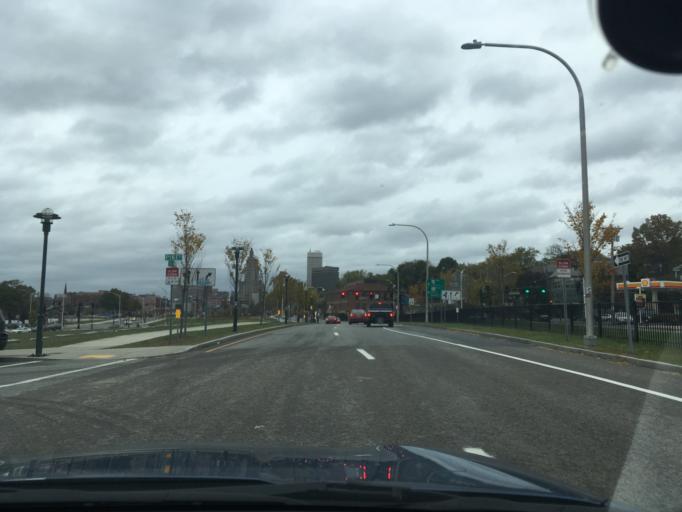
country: US
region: Rhode Island
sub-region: Providence County
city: Providence
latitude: 41.8181
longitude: -71.3998
